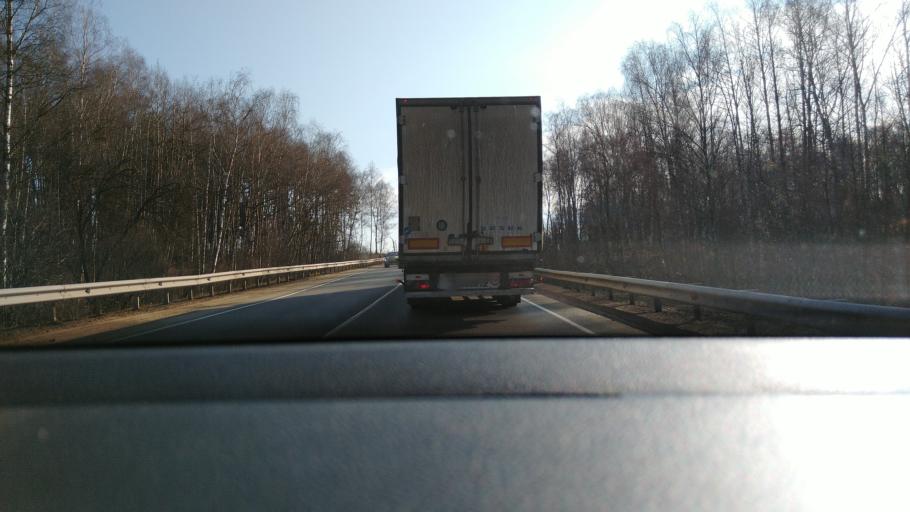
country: RU
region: Moskovskaya
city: Dubrovitsy
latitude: 55.3729
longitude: 37.4130
